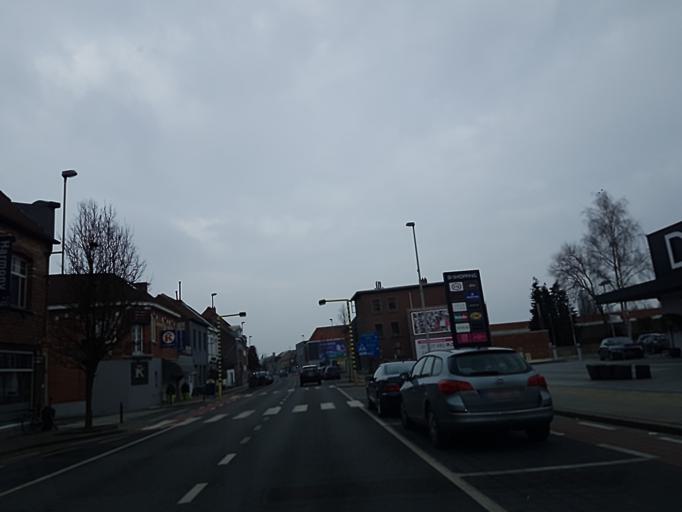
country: BE
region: Flanders
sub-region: Provincie Oost-Vlaanderen
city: Deinze
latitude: 50.9841
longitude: 3.5321
